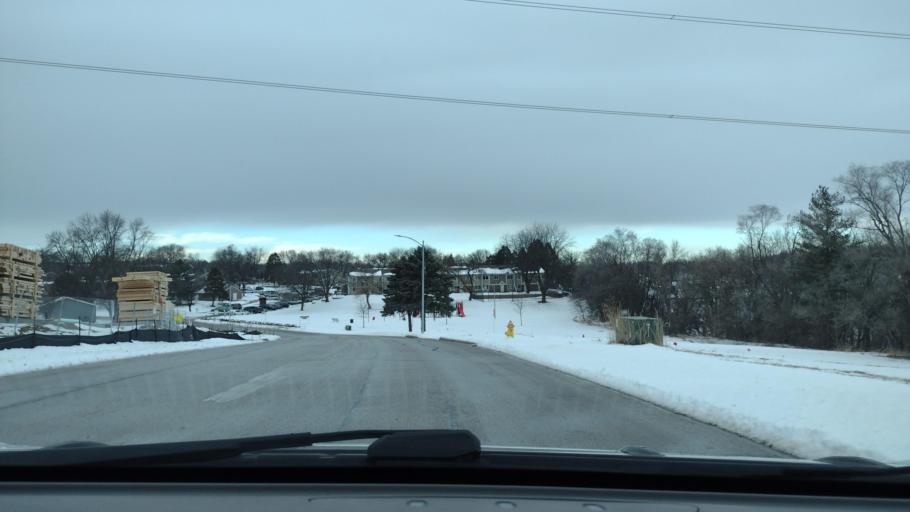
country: US
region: Nebraska
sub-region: Sarpy County
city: Bellevue
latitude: 41.1783
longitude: -95.9320
